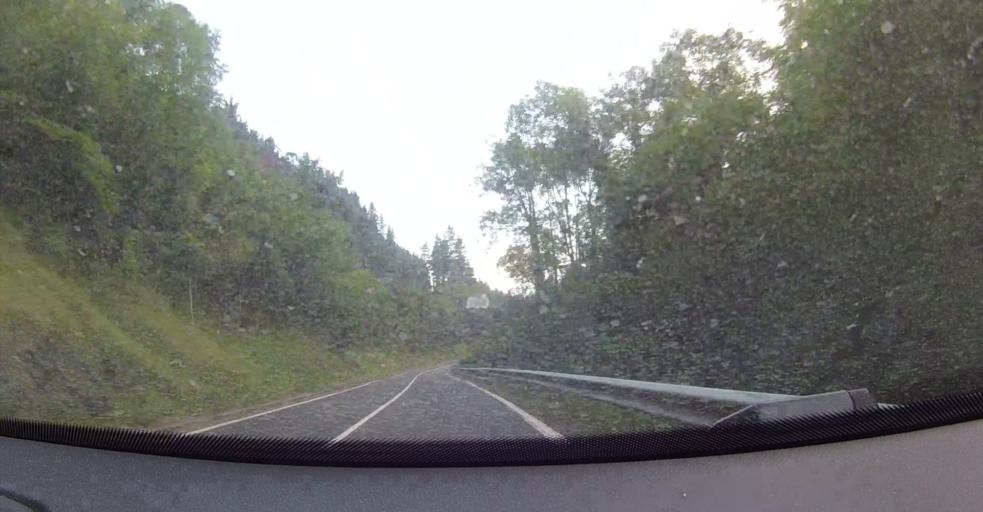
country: ES
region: Basque Country
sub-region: Bizkaia
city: Urrestieta
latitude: 43.2441
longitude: -3.1543
